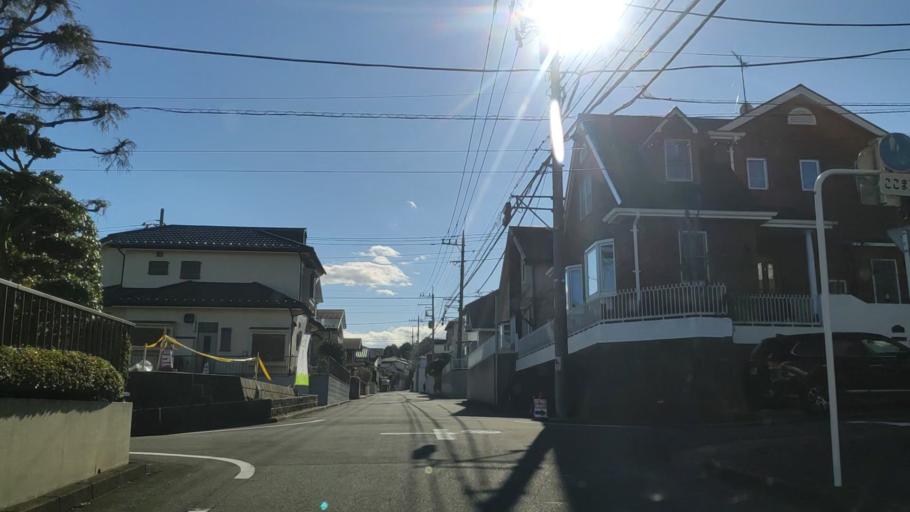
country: JP
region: Kanagawa
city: Minami-rinkan
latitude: 35.5085
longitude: 139.5257
